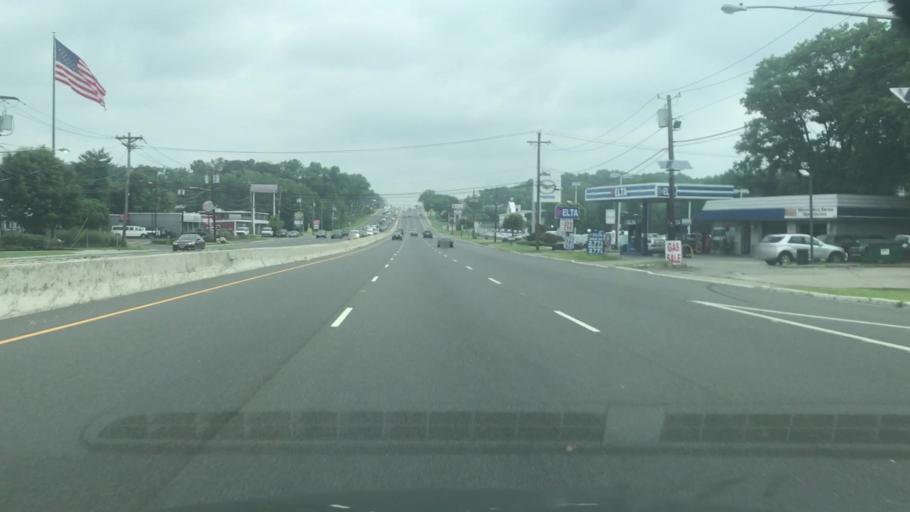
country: US
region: New Jersey
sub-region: Passaic County
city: Wayne
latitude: 40.9254
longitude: -74.2683
